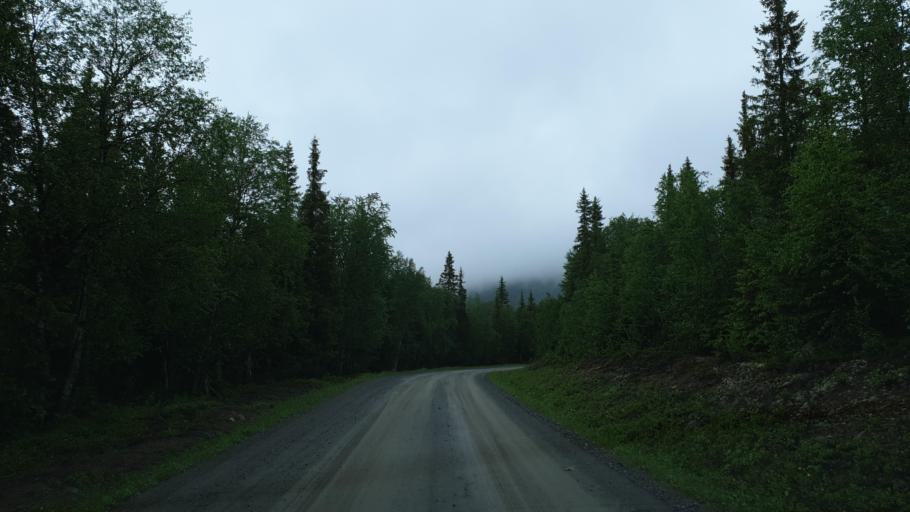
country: SE
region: Vaesterbotten
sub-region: Vilhelmina Kommun
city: Sjoberg
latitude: 65.3397
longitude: 15.8724
